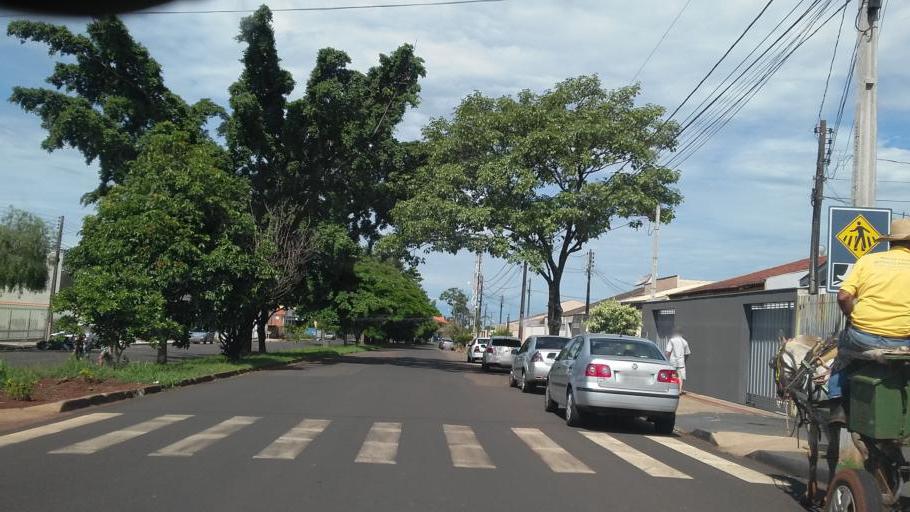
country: BR
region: Parana
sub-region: Londrina
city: Londrina
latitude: -23.2840
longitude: -51.2006
